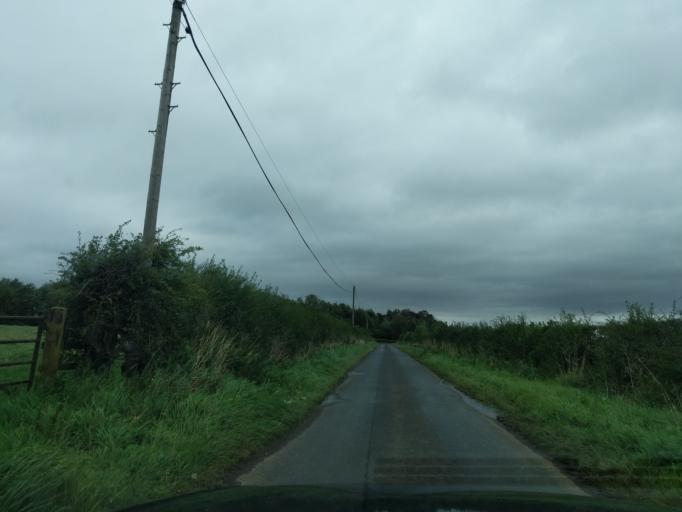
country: GB
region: Scotland
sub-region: The Scottish Borders
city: Kelso
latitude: 55.6043
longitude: -2.5035
